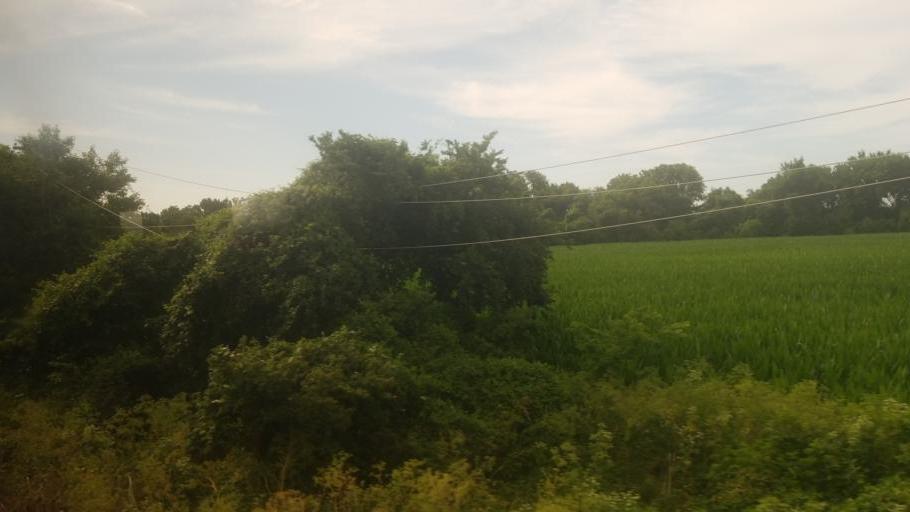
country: US
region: Kansas
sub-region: Douglas County
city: Lawrence
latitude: 38.9500
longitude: -95.1731
